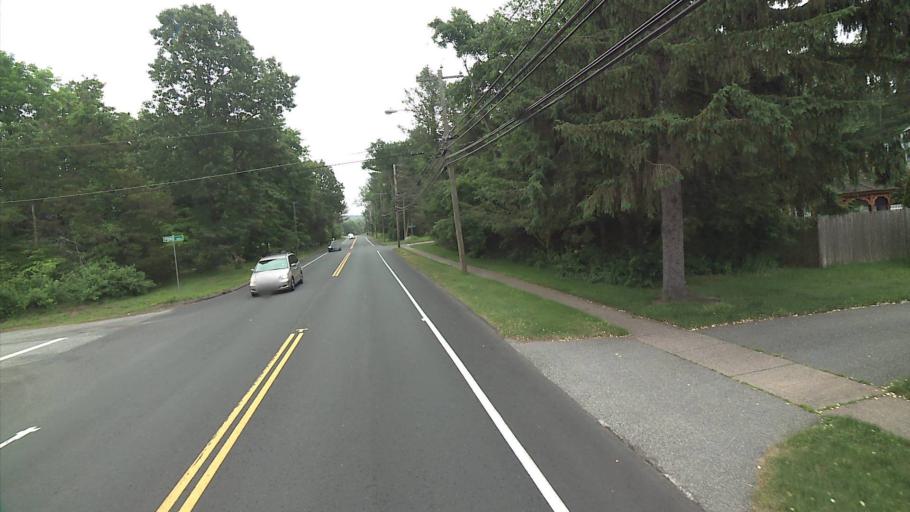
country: US
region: Connecticut
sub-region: Hartford County
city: Glastonbury Center
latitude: 41.7161
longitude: -72.5475
